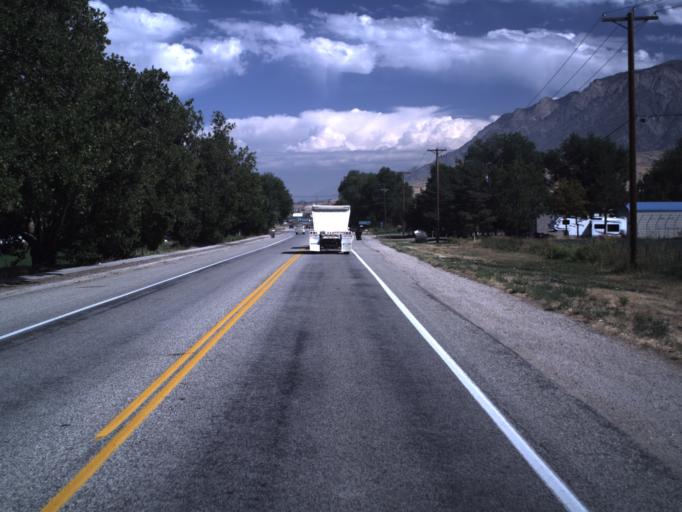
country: US
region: Utah
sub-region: Weber County
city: Farr West
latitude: 41.3096
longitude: -112.0276
